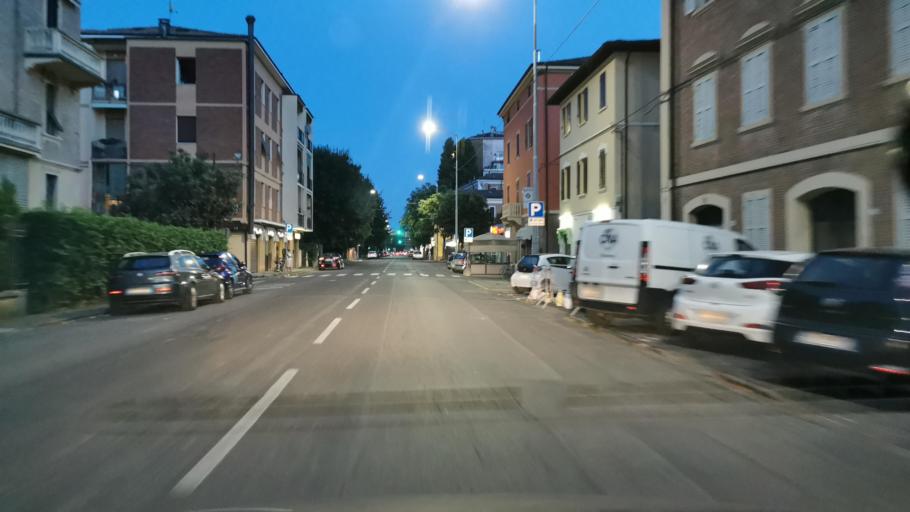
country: IT
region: Emilia-Romagna
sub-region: Provincia di Modena
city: Modena
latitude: 44.6385
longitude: 10.9320
